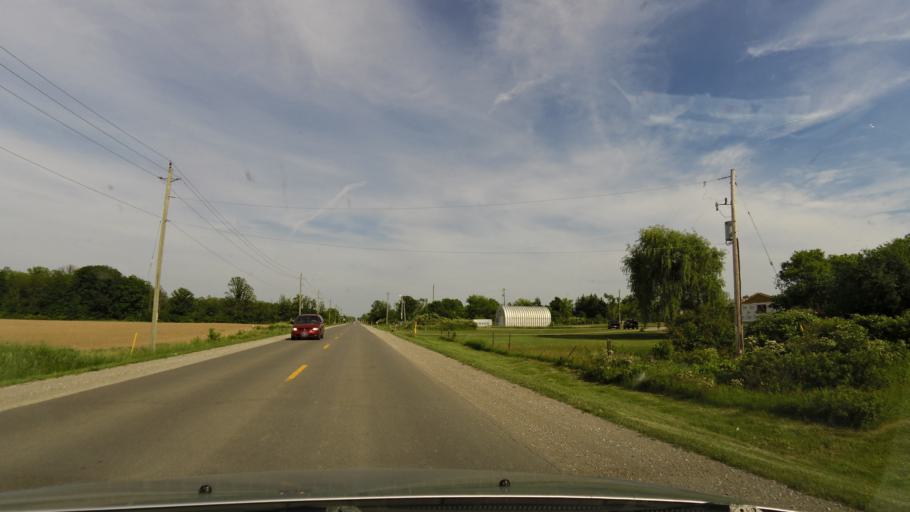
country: CA
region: Ontario
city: Brantford
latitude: 43.0613
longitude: -80.0980
